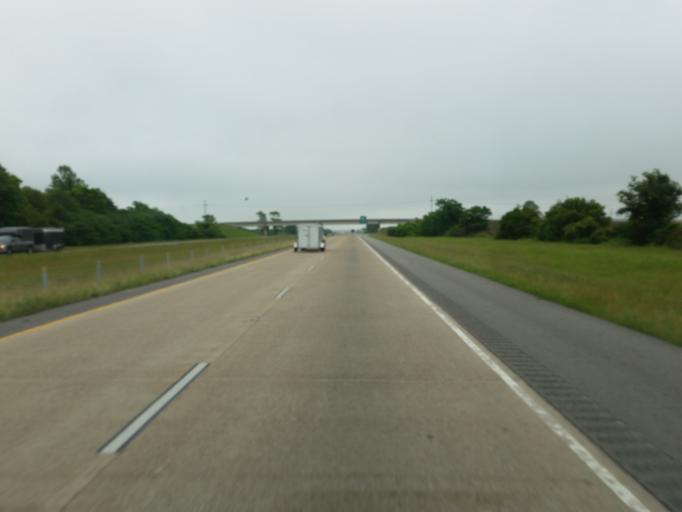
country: US
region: Mississippi
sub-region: Warren County
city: Vicksburg
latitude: 32.3303
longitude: -91.0278
